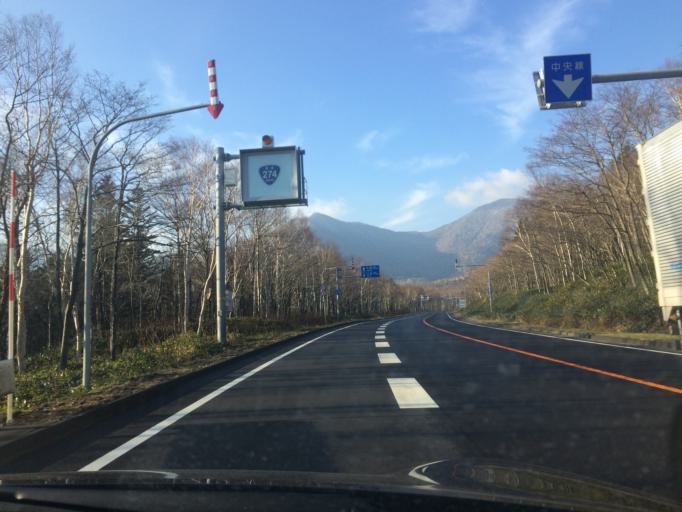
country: JP
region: Hokkaido
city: Otofuke
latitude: 42.9640
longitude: 142.7992
